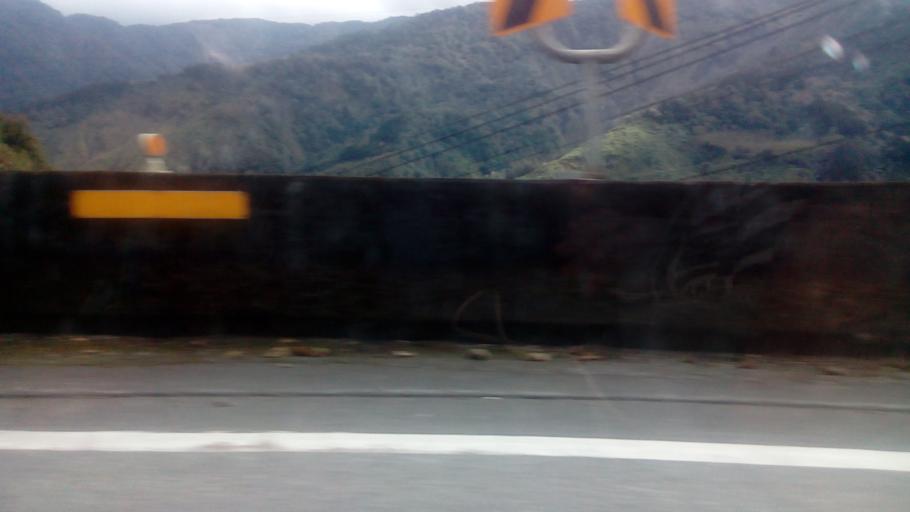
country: TW
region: Taiwan
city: Daxi
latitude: 24.4638
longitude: 121.3941
